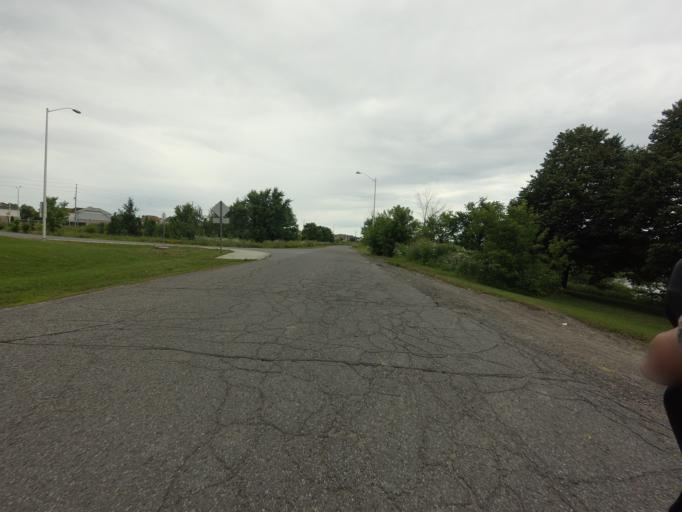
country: CA
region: Ontario
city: Bells Corners
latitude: 45.2663
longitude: -75.7064
